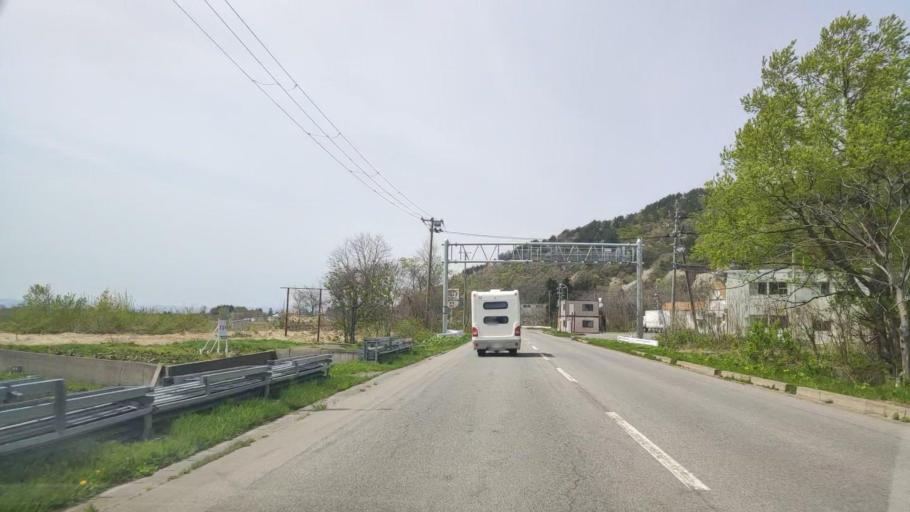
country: JP
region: Aomori
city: Aomori Shi
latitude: 40.8285
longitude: 140.8521
